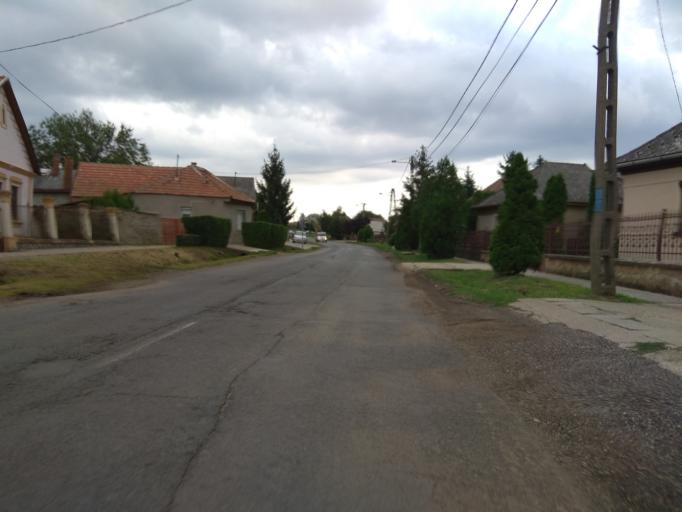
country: HU
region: Borsod-Abauj-Zemplen
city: Bekecs
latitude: 48.1576
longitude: 21.1549
